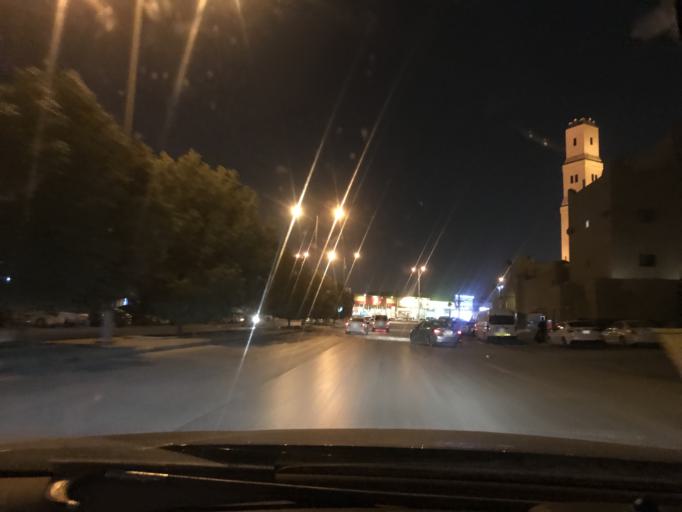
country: SA
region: Ar Riyad
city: Riyadh
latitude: 24.7474
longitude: 46.7586
